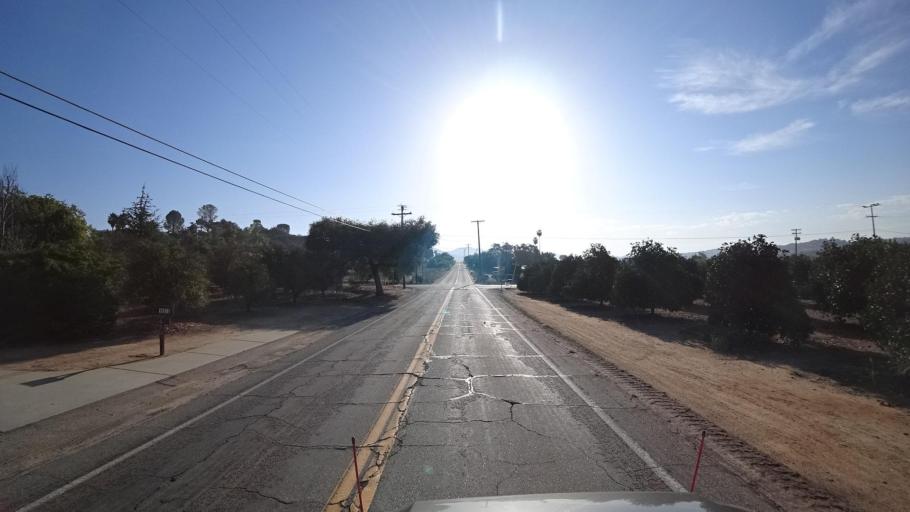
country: US
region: California
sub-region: San Diego County
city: Valley Center
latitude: 33.2357
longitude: -116.9942
